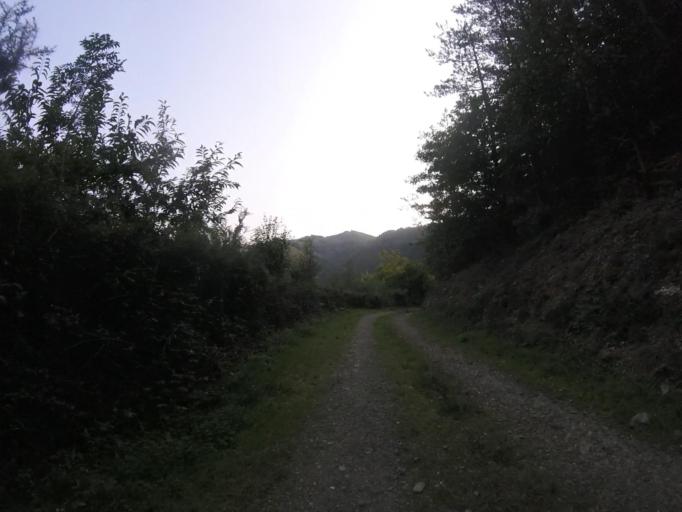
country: ES
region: Basque Country
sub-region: Provincia de Guipuzcoa
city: Errenteria
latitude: 43.2626
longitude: -1.8459
